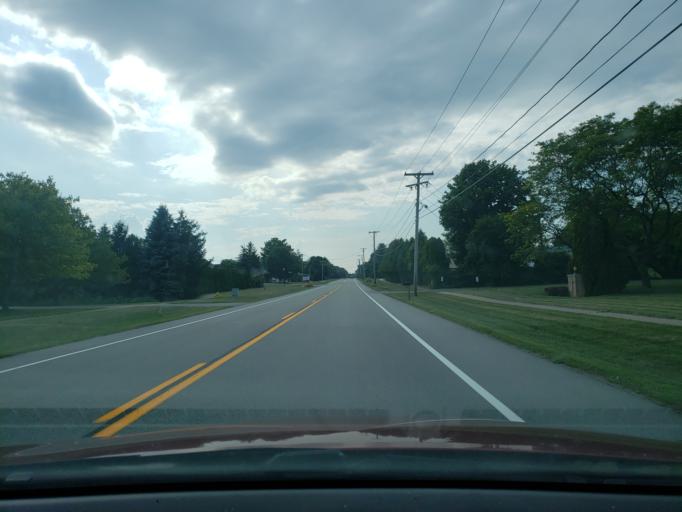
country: US
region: New York
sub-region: Monroe County
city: Greece
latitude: 43.2787
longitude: -77.7016
